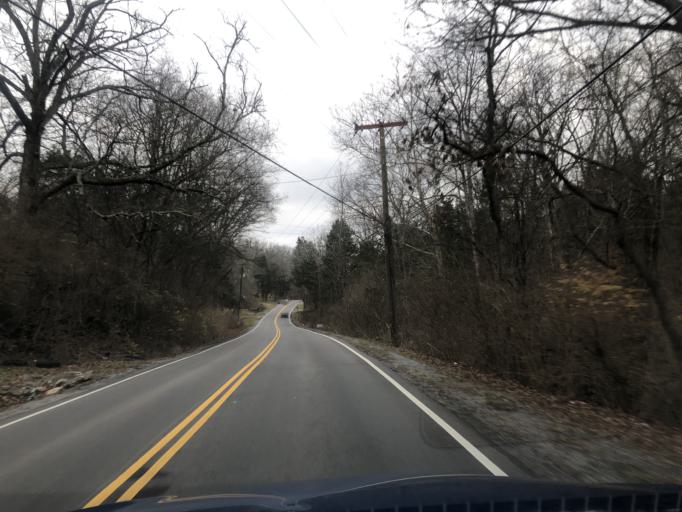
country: US
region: Tennessee
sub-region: Davidson County
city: Belle Meade
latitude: 36.1001
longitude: -86.9320
